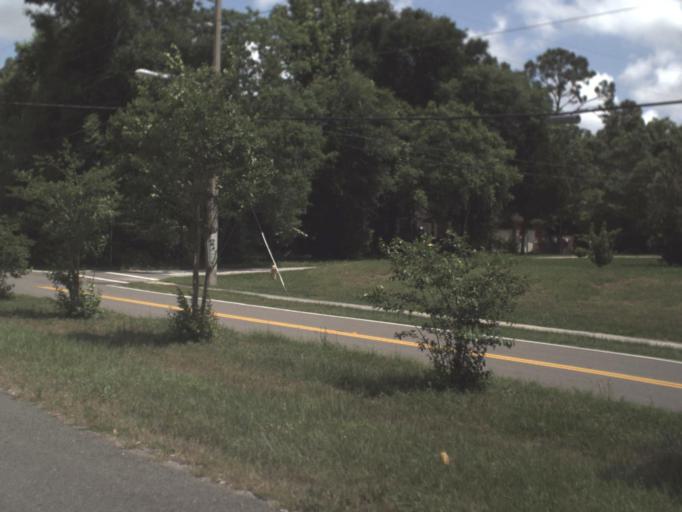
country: US
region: Florida
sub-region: Duval County
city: Jacksonville
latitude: 30.2953
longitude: -81.5585
